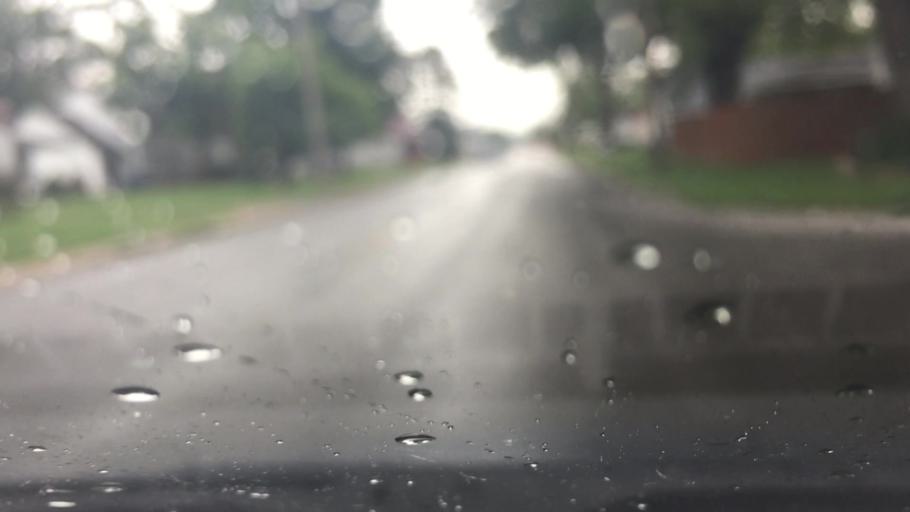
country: US
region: Illinois
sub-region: Williamson County
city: Marion
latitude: 37.7283
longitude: -88.9464
